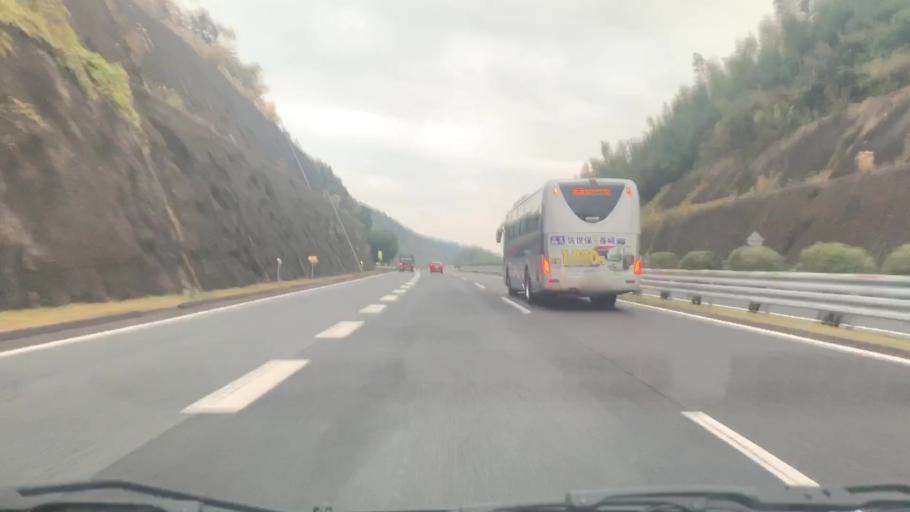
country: JP
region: Nagasaki
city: Omura
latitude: 32.9932
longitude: 129.9535
